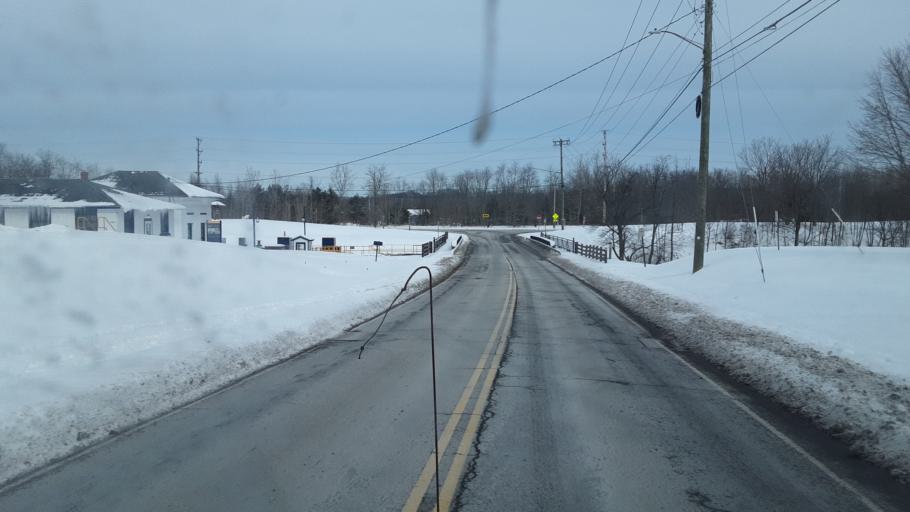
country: US
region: New York
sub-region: Wayne County
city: Newark
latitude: 43.0462
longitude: -77.0840
